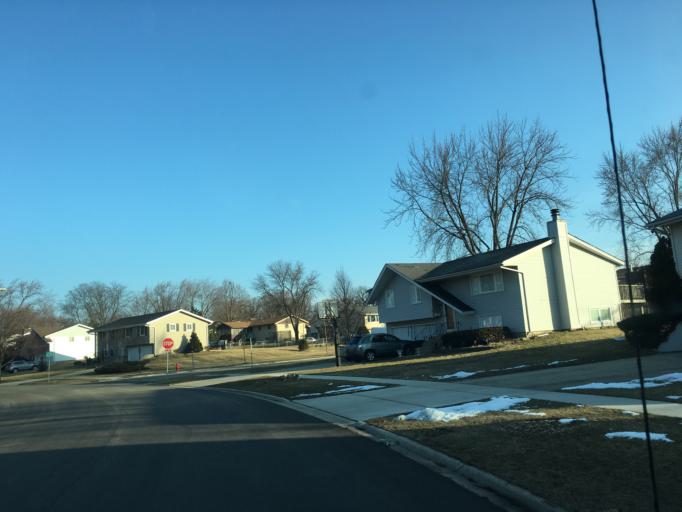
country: US
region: Illinois
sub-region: Cook County
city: Schaumburg
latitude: 42.0223
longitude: -88.0956
